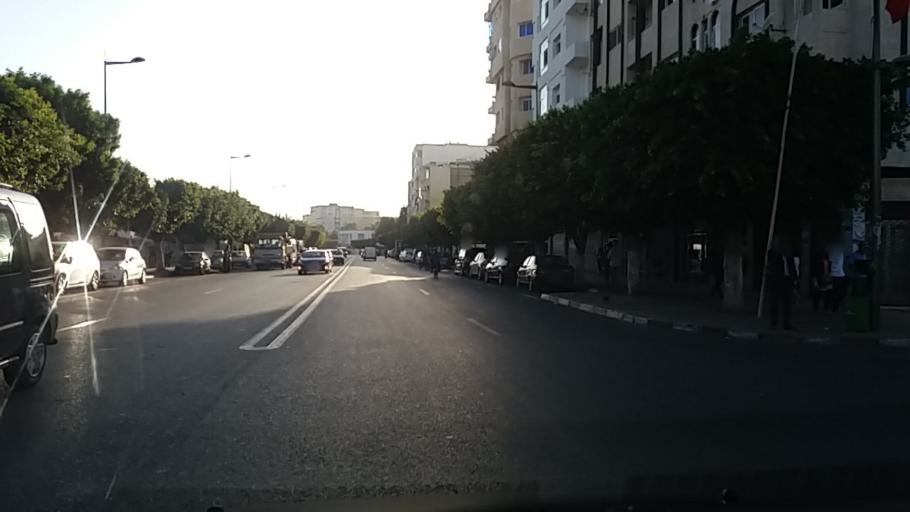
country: MA
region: Gharb-Chrarda-Beni Hssen
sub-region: Kenitra Province
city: Kenitra
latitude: 34.2631
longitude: -6.5737
